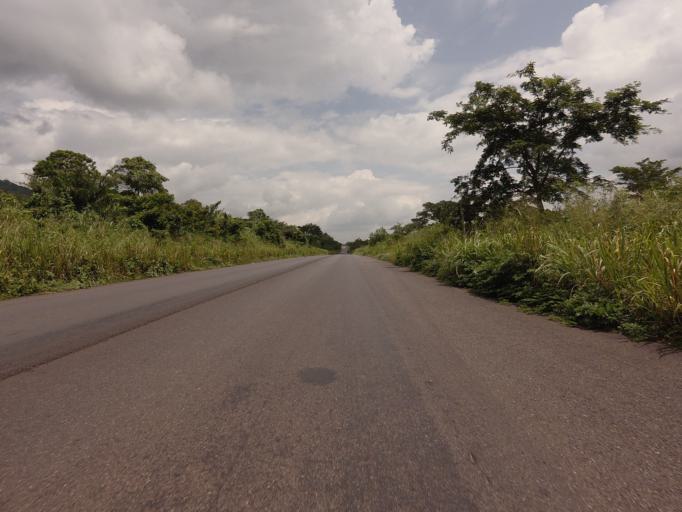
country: GH
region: Volta
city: Ho
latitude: 6.5626
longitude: 0.2656
